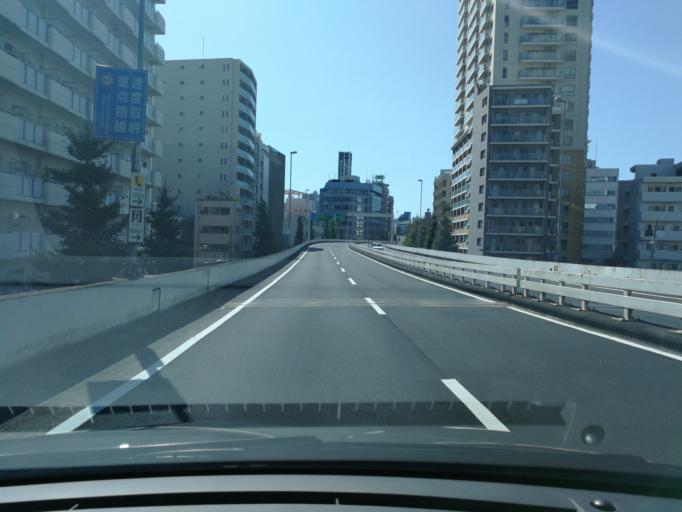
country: JP
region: Tokyo
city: Tokyo
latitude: 35.6270
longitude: 139.7194
